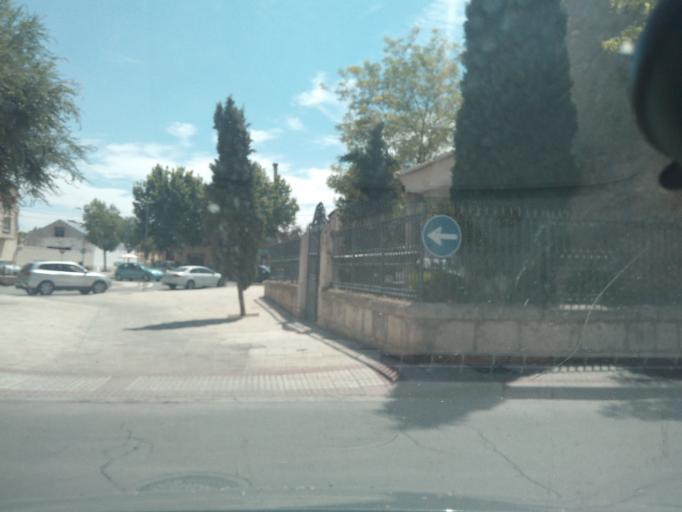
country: ES
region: Castille-La Mancha
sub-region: Province of Toledo
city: Villacanas
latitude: 39.6221
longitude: -3.3335
